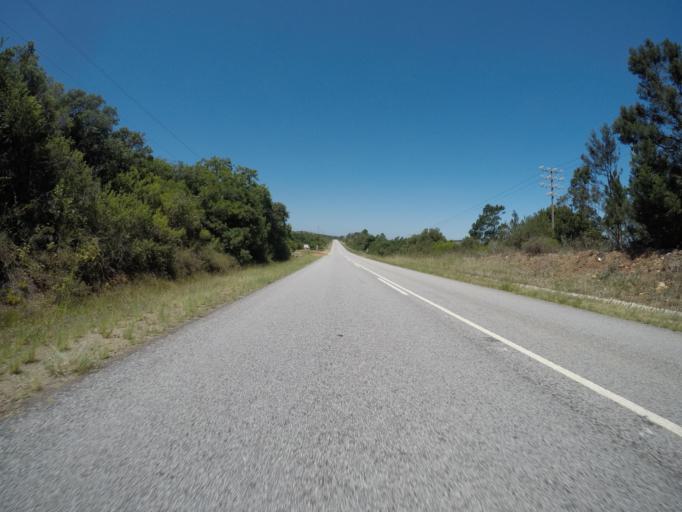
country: ZA
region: Eastern Cape
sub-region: Cacadu District Municipality
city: Kareedouw
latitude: -33.9593
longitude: 24.4125
